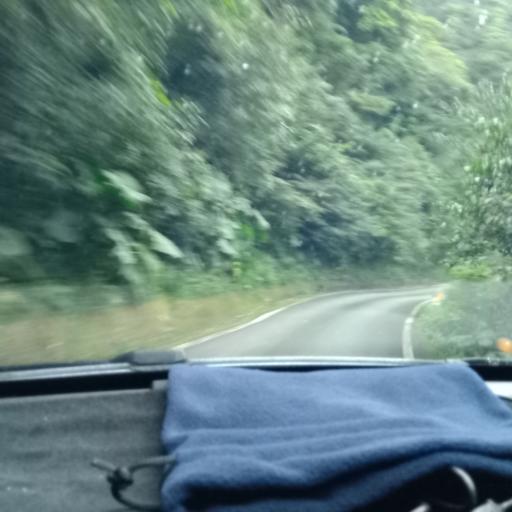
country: TW
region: Taiwan
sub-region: Yilan
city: Yilan
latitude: 24.8123
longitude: 121.7009
